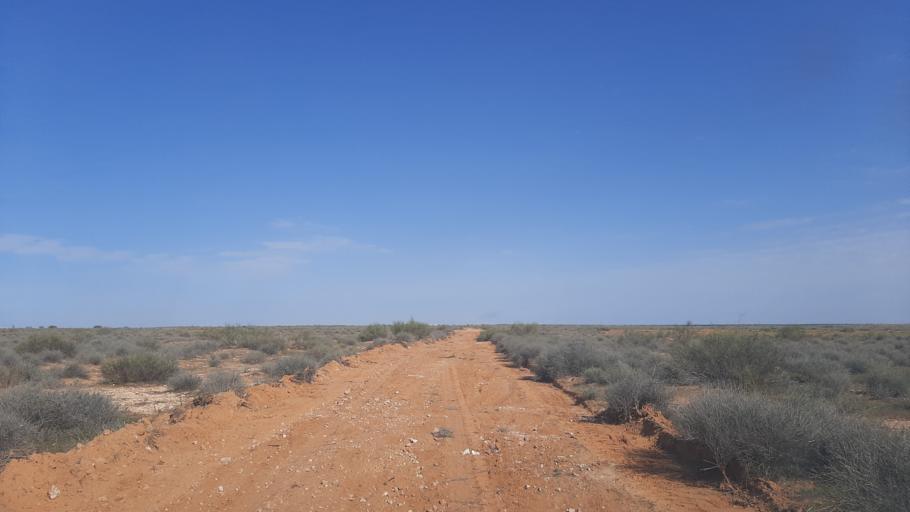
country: TN
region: Madanin
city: Medenine
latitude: 33.2447
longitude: 10.7427
